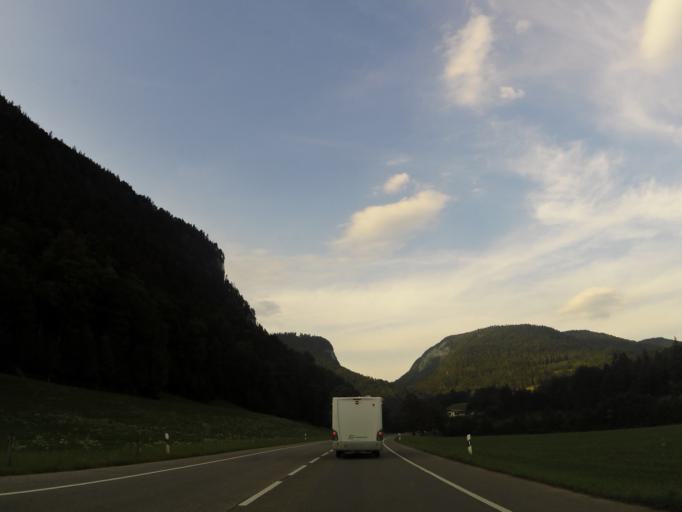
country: DE
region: Bavaria
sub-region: Upper Bavaria
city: Berchtesgaden
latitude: 47.6471
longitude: 13.0310
